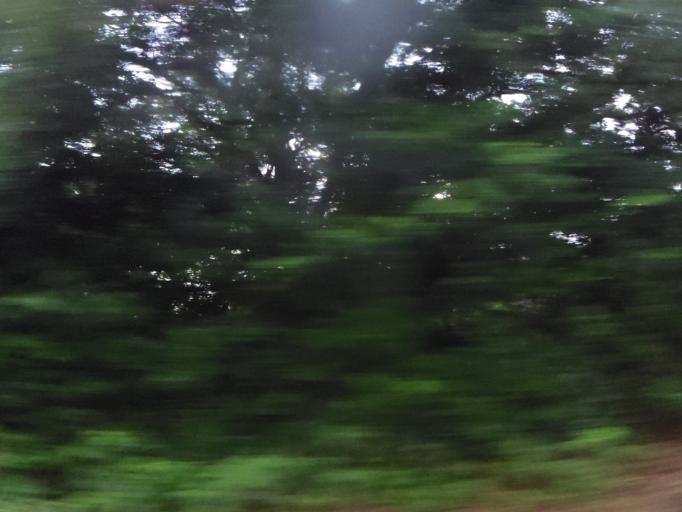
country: US
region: Florida
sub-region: Duval County
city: Jacksonville
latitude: 30.2664
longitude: -81.5816
